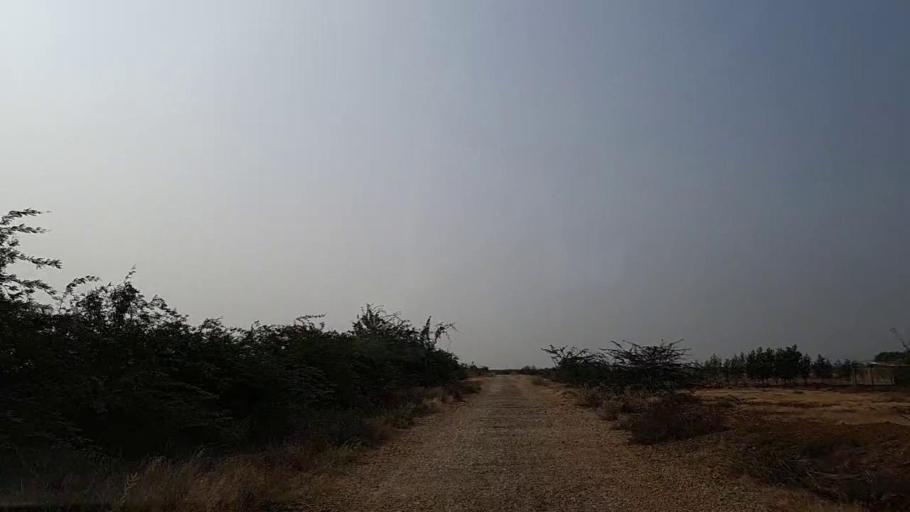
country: PK
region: Sindh
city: Thatta
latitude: 24.7241
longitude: 67.8329
